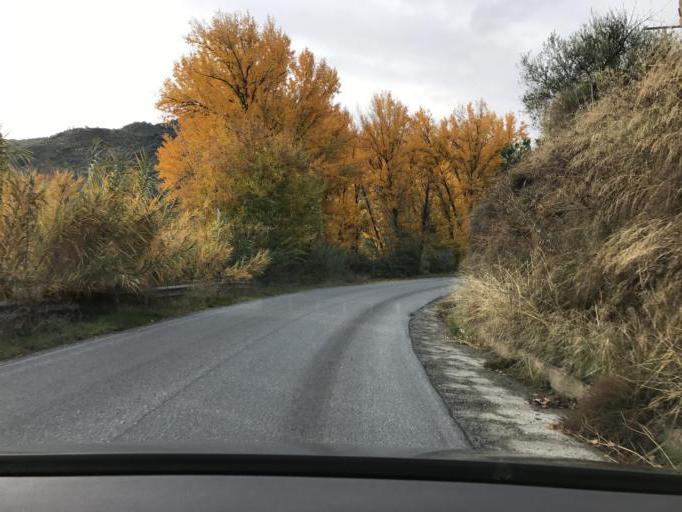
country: ES
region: Andalusia
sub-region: Provincia de Granada
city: Pinos Genil
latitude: 37.1643
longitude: -3.5163
